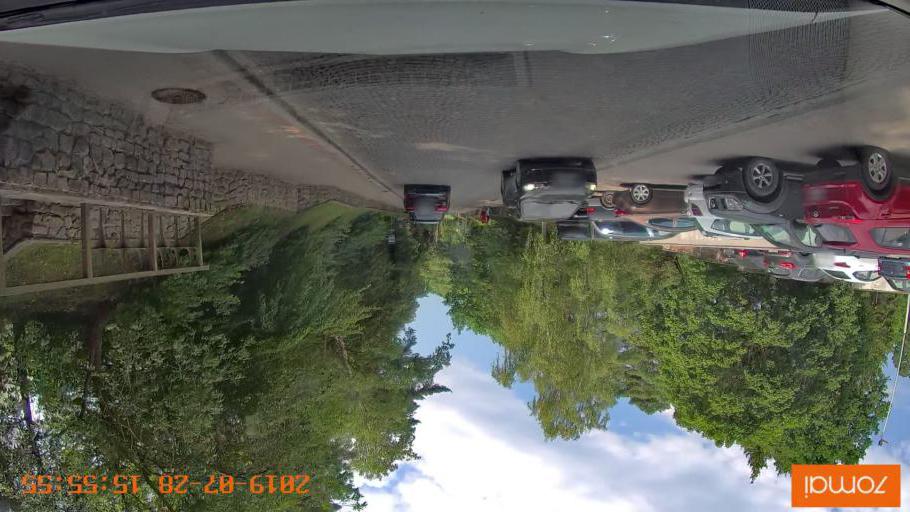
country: RU
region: Kaliningrad
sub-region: Gorod Svetlogorsk
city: Svetlogorsk
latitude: 54.9405
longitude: 20.1429
